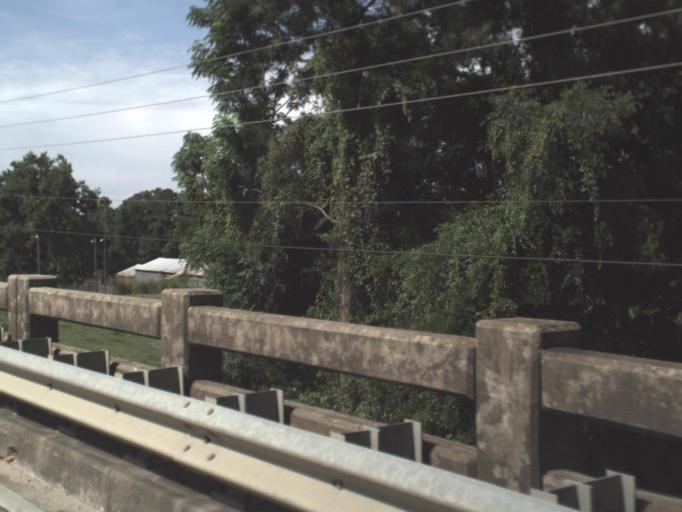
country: US
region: Florida
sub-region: Madison County
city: Madison
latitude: 30.4581
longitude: -83.4095
